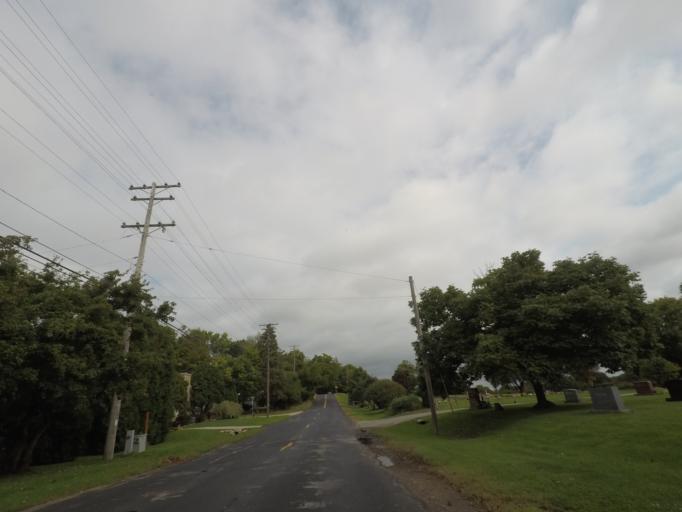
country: US
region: Wisconsin
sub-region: Dane County
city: Shorewood Hills
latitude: 43.0647
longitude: -89.4363
